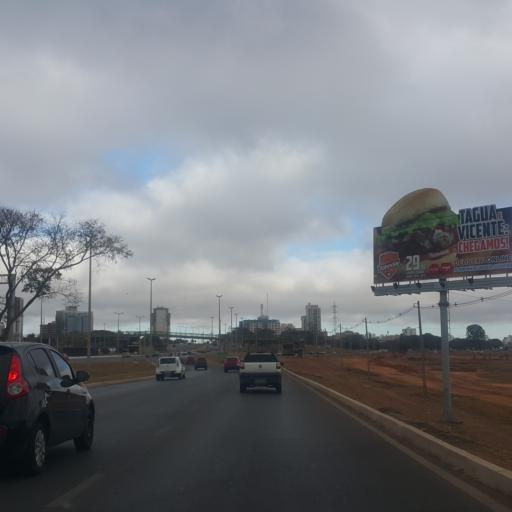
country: BR
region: Federal District
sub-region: Brasilia
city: Brasilia
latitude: -15.8305
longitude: -48.0442
